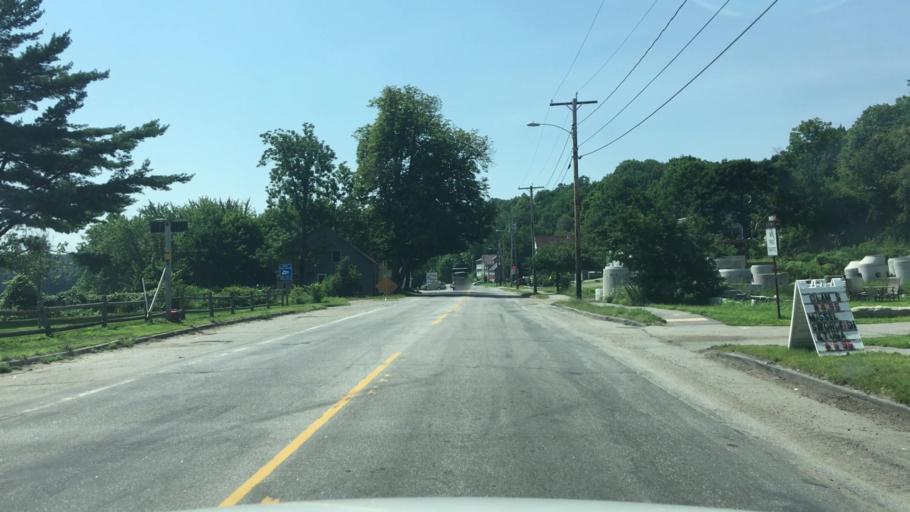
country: US
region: Maine
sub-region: Kennebec County
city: Hallowell
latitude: 44.2833
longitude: -69.7912
